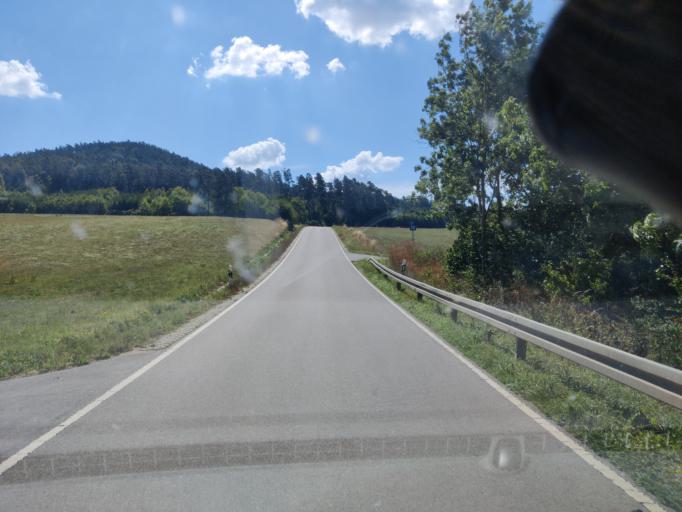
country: DE
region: Bavaria
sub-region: Regierungsbezirk Mittelfranken
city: Bergen
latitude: 49.0940
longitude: 11.1460
